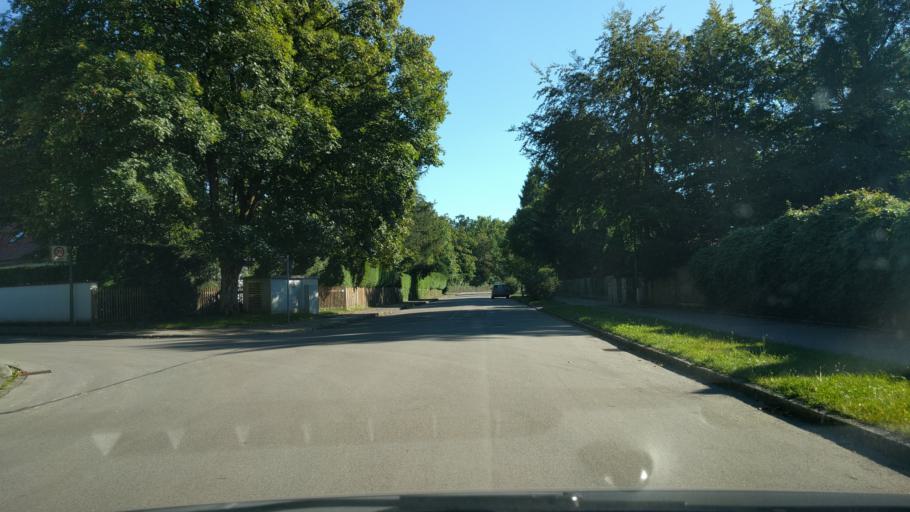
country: DE
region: Bavaria
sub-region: Upper Bavaria
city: Pullach im Isartal
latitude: 48.0524
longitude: 11.5292
